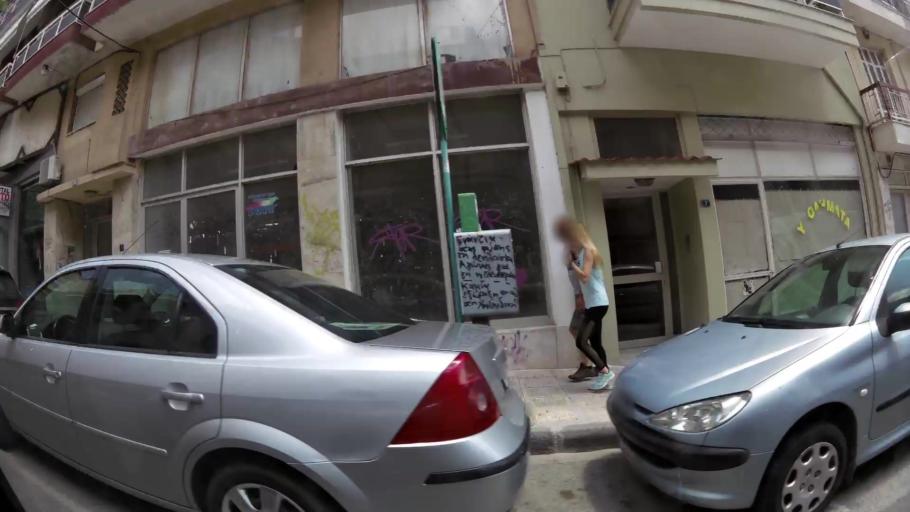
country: GR
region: West Macedonia
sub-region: Nomos Kozanis
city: Kozani
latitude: 40.2985
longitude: 21.7905
